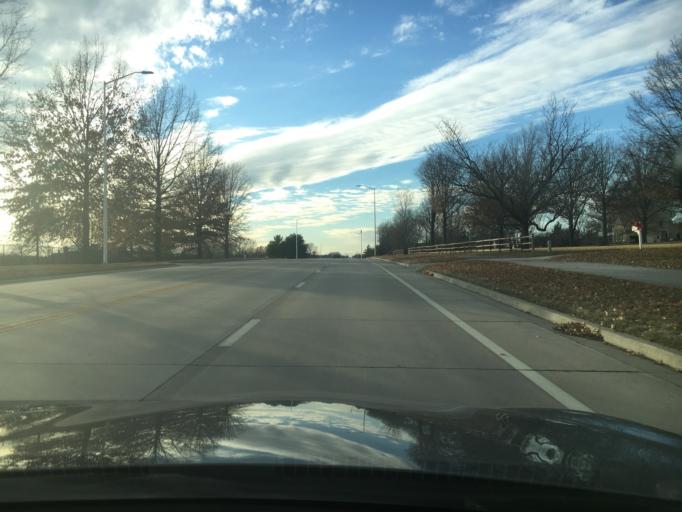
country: US
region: Kansas
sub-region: Johnson County
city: Leawood
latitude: 38.8693
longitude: -94.6323
